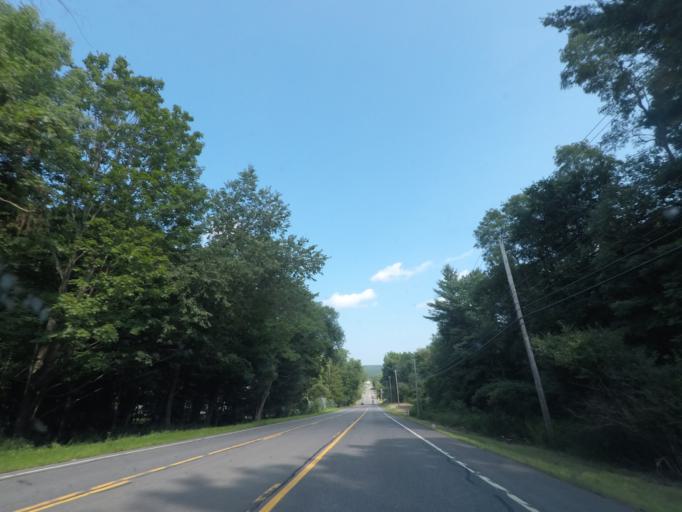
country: US
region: New York
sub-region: Rensselaer County
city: Nassau
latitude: 42.5203
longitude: -73.6334
